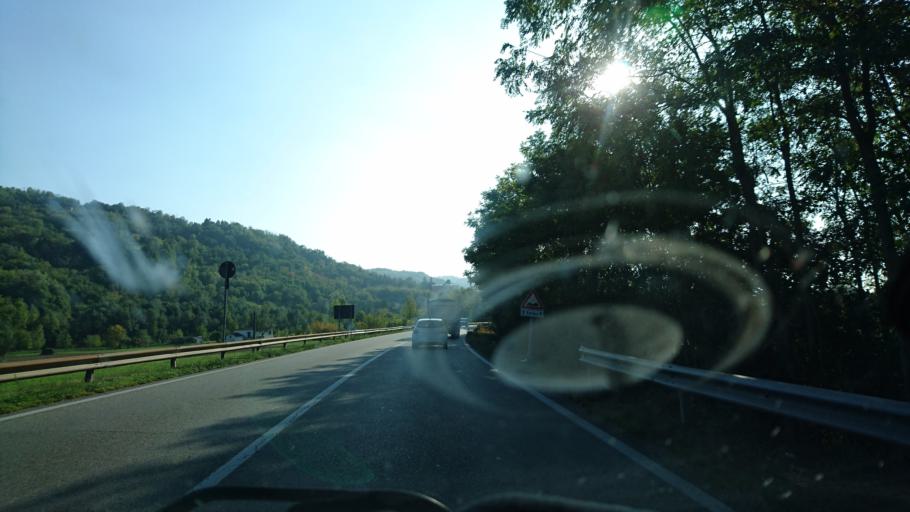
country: IT
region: Piedmont
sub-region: Provincia di Alessandria
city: Acqui Terme
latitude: 44.6684
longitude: 8.4802
